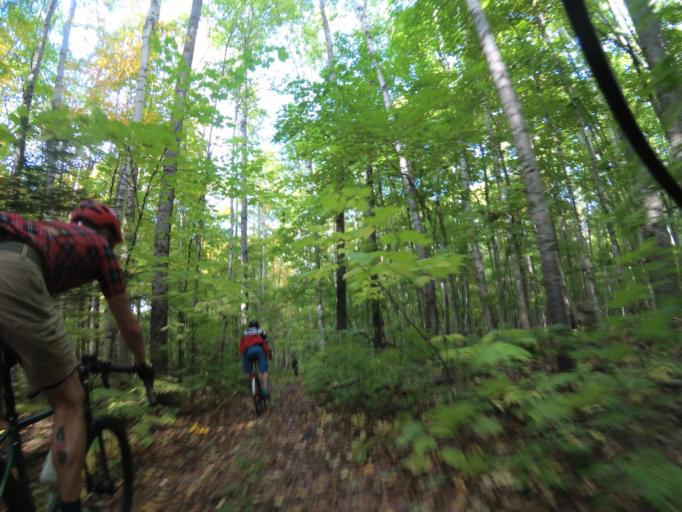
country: CA
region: Ontario
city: Pembroke
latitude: 45.3287
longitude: -77.1812
